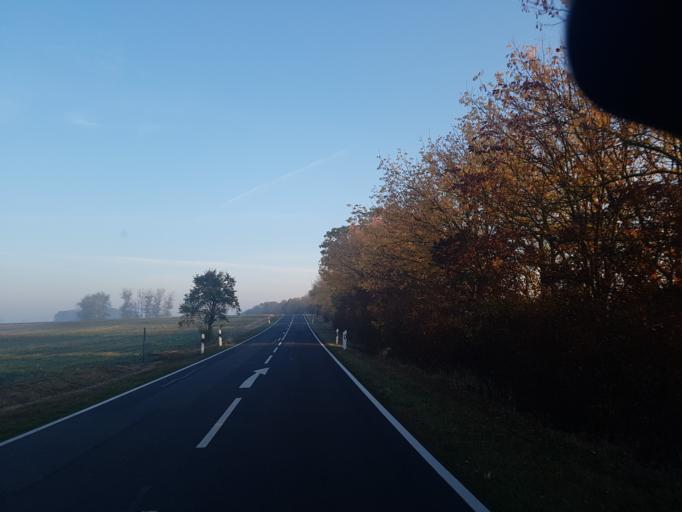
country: DE
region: Brandenburg
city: Juterbog
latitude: 51.9250
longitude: 13.0877
